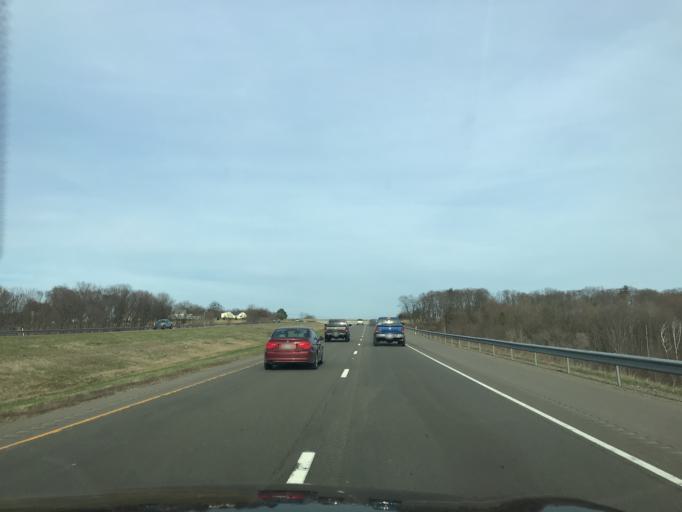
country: US
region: Pennsylvania
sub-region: Lycoming County
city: Montoursville
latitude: 41.2527
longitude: -76.8685
